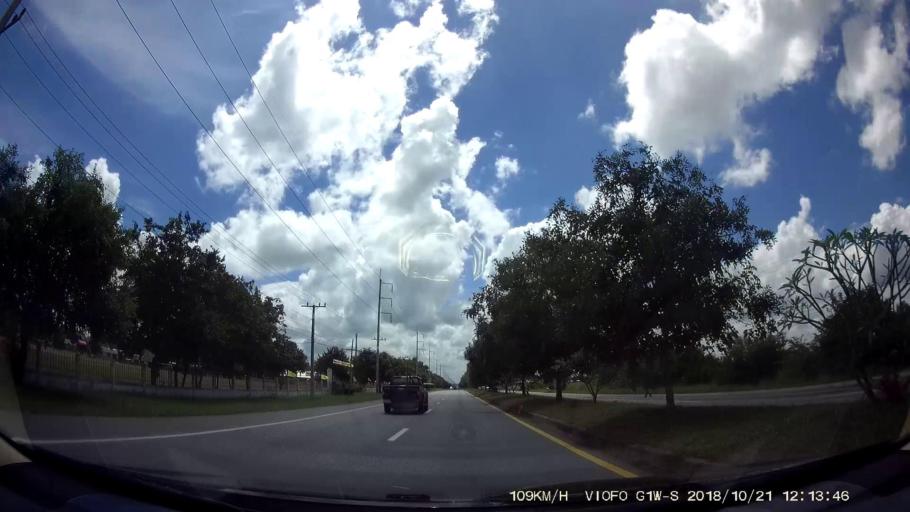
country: TH
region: Chaiyaphum
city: Chatturat
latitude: 15.3878
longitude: 101.8384
